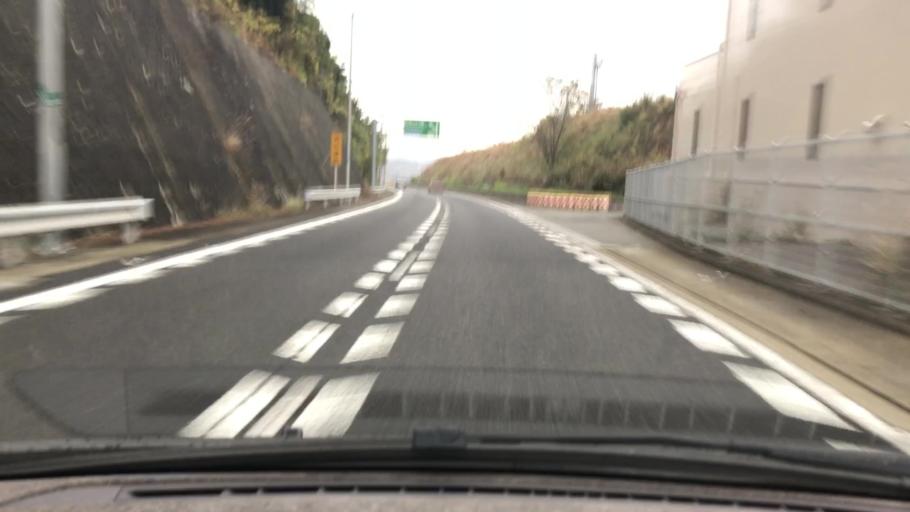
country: JP
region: Hyogo
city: Sandacho
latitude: 34.8107
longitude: 135.2471
